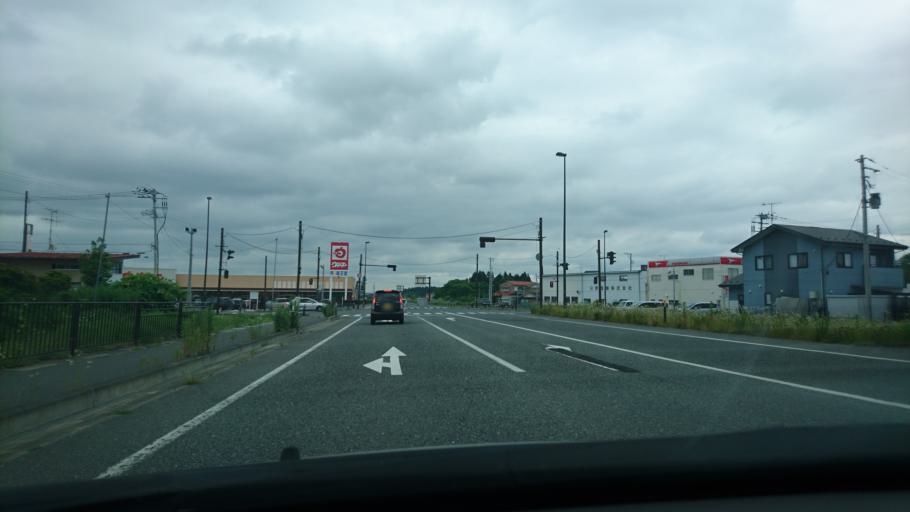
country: JP
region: Miyagi
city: Furukawa
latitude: 38.7331
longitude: 141.0352
